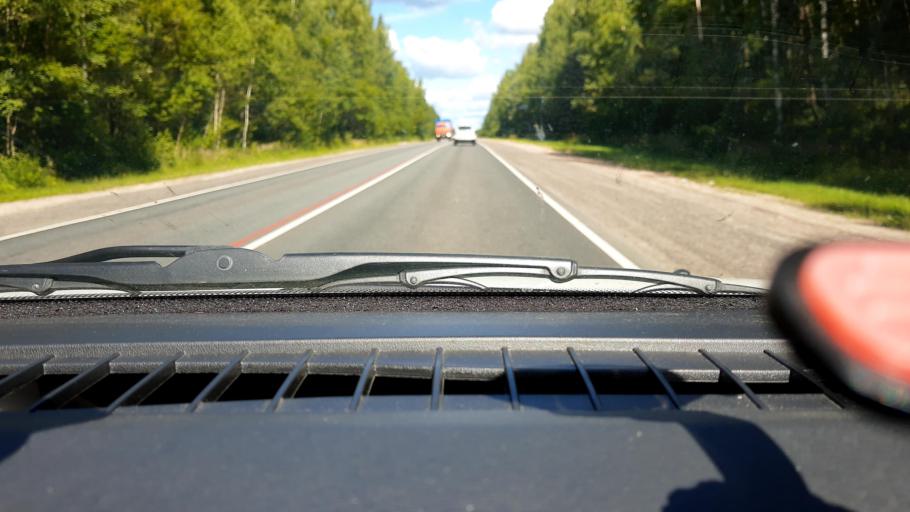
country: RU
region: Nizjnij Novgorod
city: Arzamas
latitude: 55.4332
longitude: 43.8992
